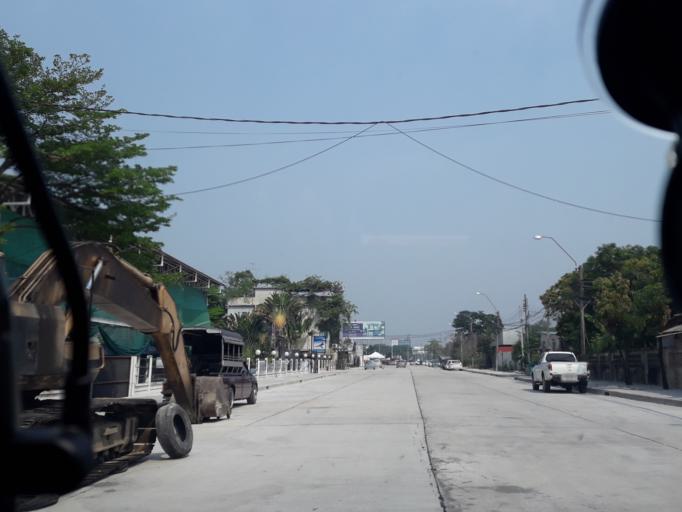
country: TH
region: Bangkok
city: Lat Phrao
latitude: 13.8219
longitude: 100.6286
